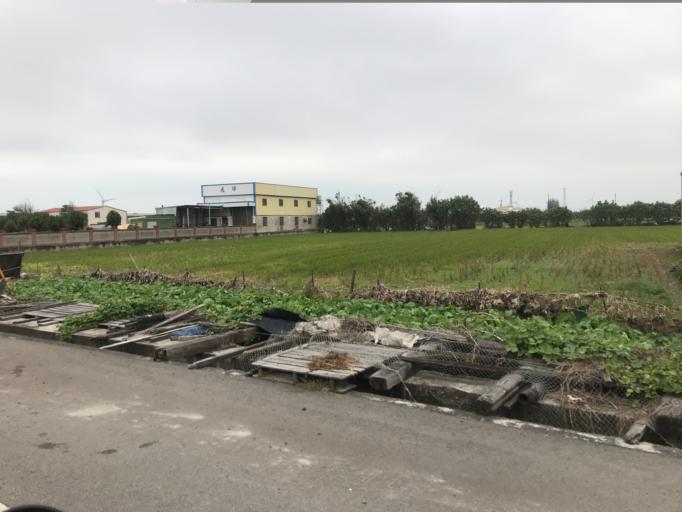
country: TW
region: Taiwan
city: Fengyuan
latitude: 24.3762
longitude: 120.5945
